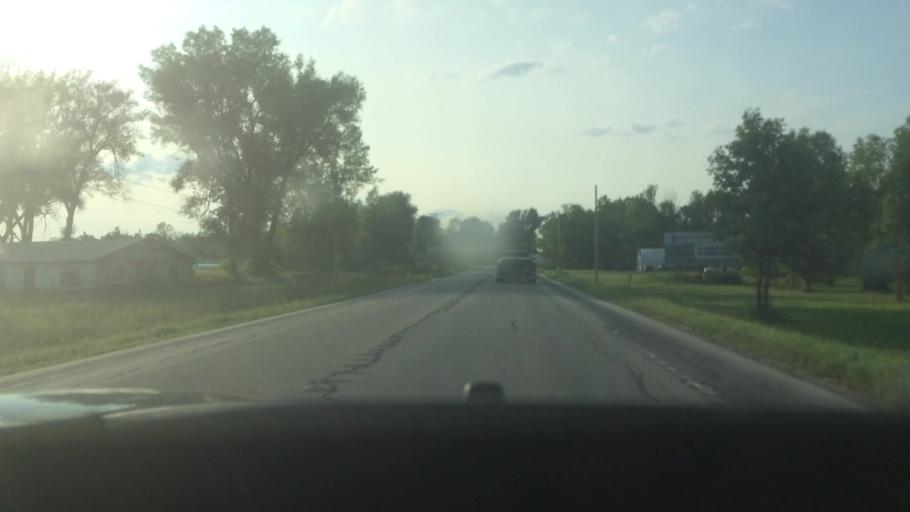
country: US
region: New York
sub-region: St. Lawrence County
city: Ogdensburg
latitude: 44.6747
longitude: -75.4344
